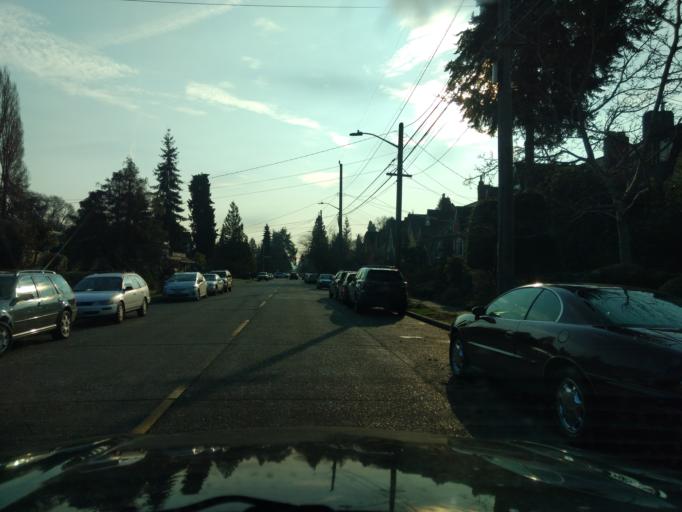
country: US
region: Washington
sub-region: King County
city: Lake Forest Park
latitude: 47.6844
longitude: -122.3068
